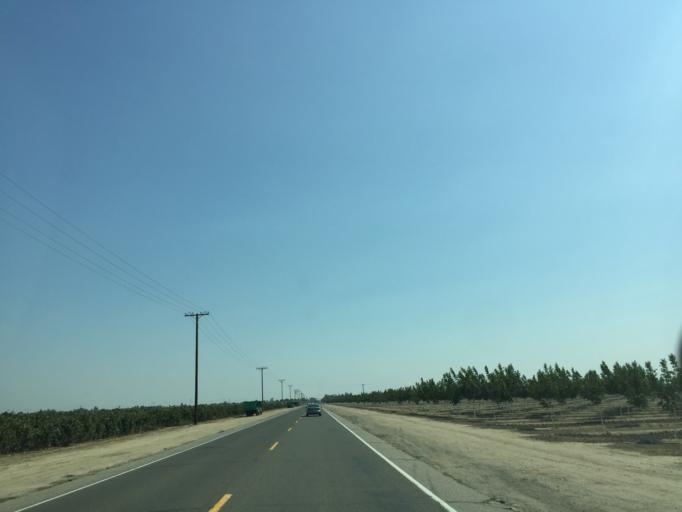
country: US
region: California
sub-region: Kings County
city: Lucerne
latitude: 36.3644
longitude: -119.6730
